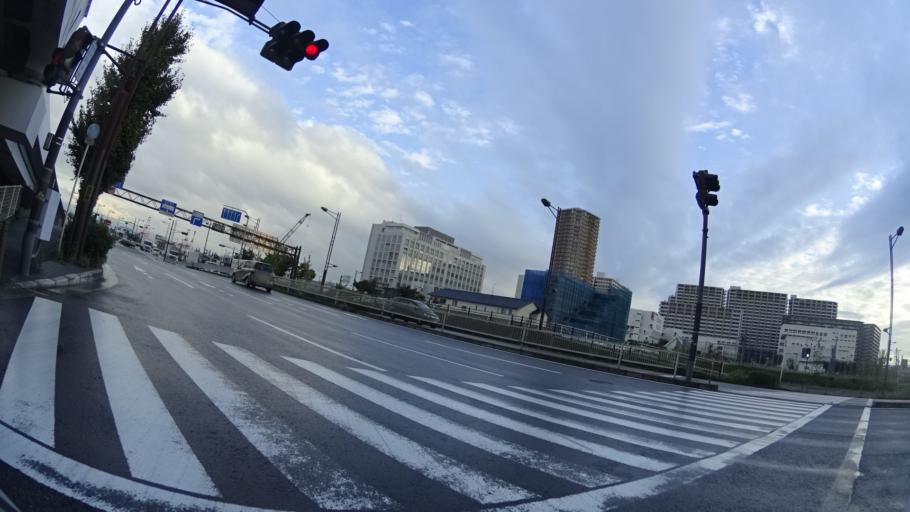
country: JP
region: Hyogo
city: Amagasaki
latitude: 34.6394
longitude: 135.4115
